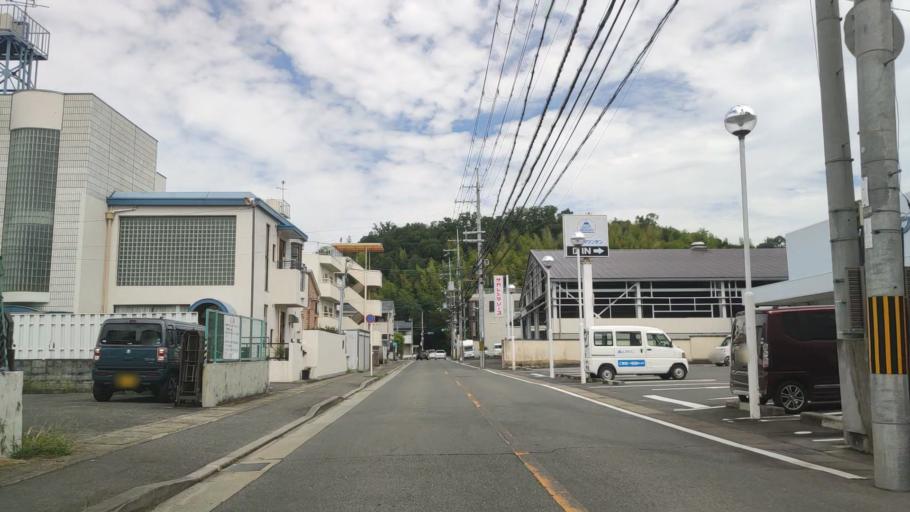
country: JP
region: Kyoto
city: Kyoto
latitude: 35.0223
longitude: 135.6982
